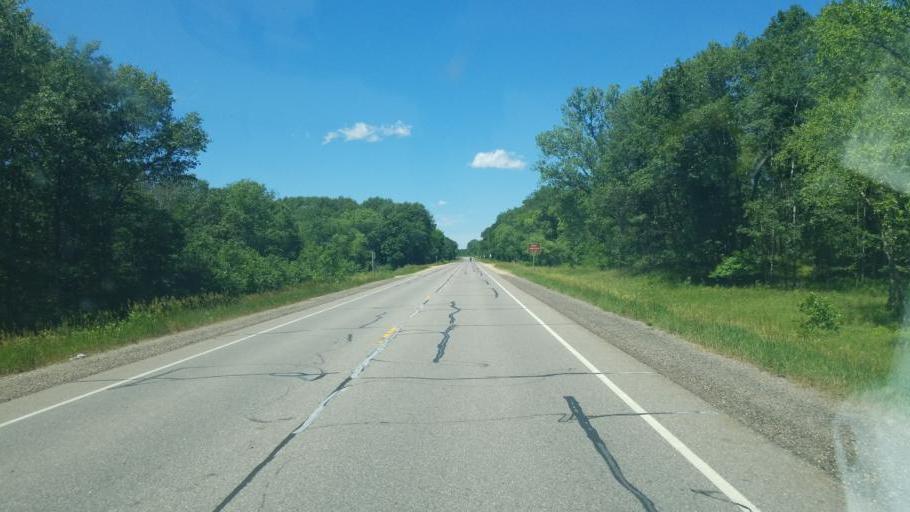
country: US
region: Wisconsin
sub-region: Adams County
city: Friendship
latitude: 44.0475
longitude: -90.0042
